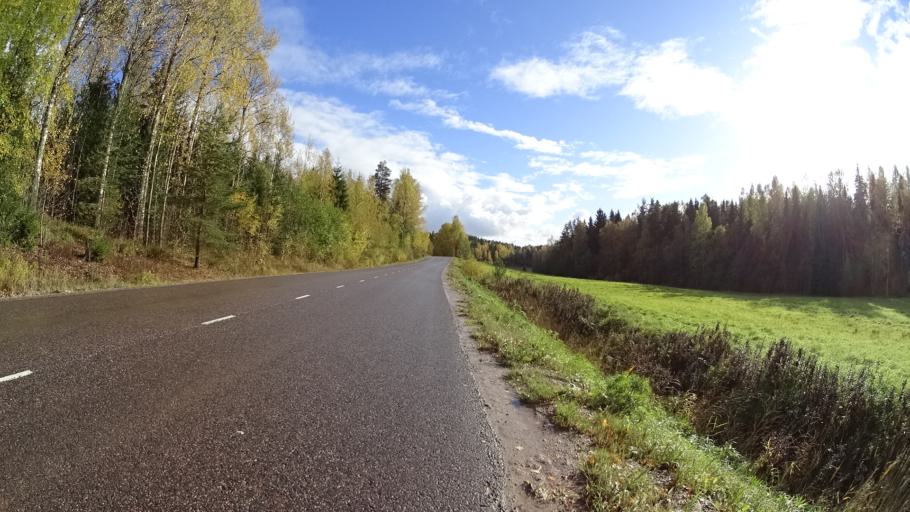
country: FI
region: Uusimaa
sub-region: Helsinki
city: Kilo
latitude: 60.2917
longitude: 24.8019
